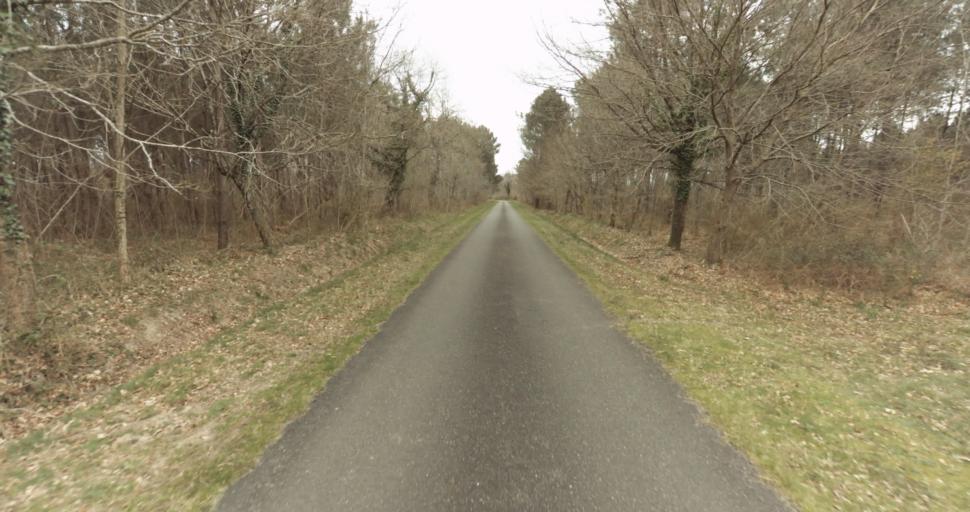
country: FR
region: Aquitaine
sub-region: Departement des Landes
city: Roquefort
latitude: 44.0661
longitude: -0.3861
